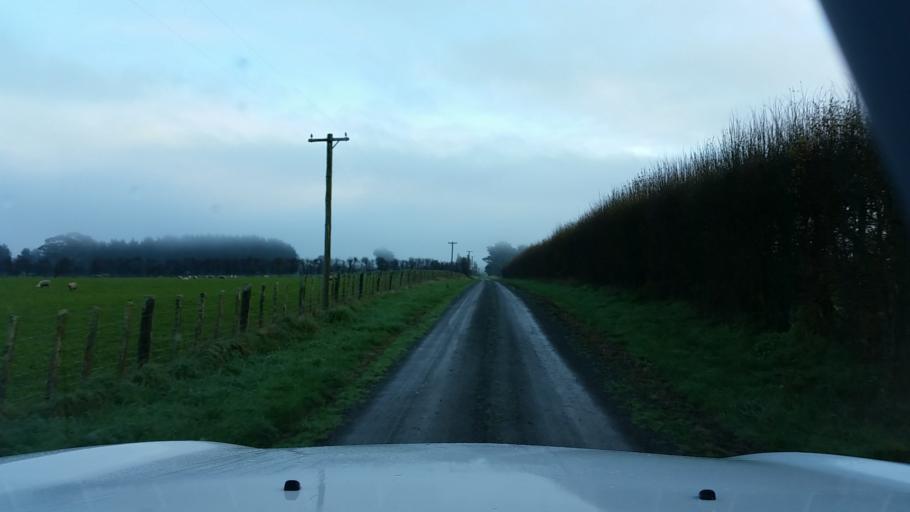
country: NZ
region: Wellington
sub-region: Masterton District
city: Masterton
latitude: -41.0824
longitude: 175.6629
